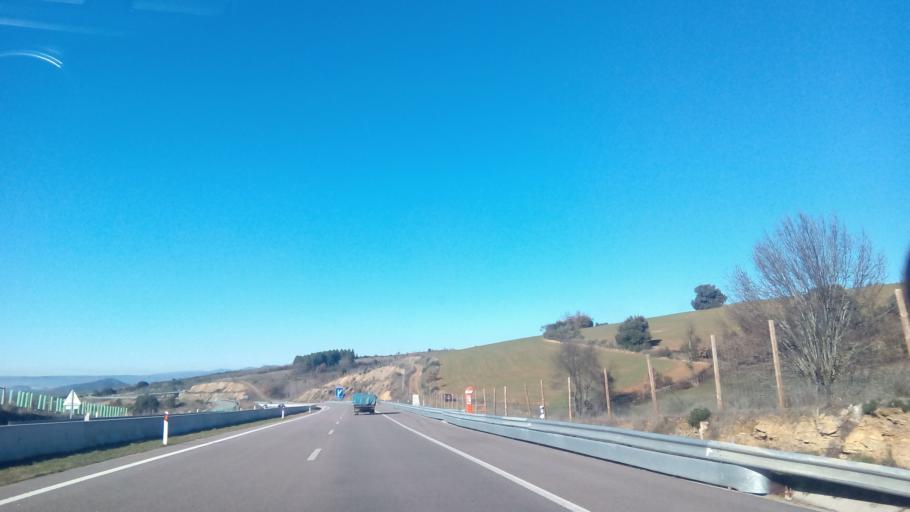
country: ES
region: Castille and Leon
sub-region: Provincia de Zamora
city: Trabazos
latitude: 41.7504
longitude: -6.6291
